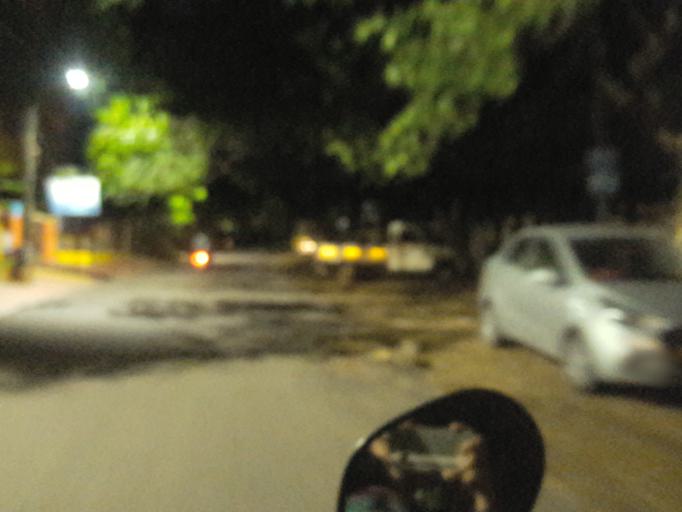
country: IN
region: Telangana
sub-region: Rangareddi
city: Kukatpalli
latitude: 17.4787
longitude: 78.3933
